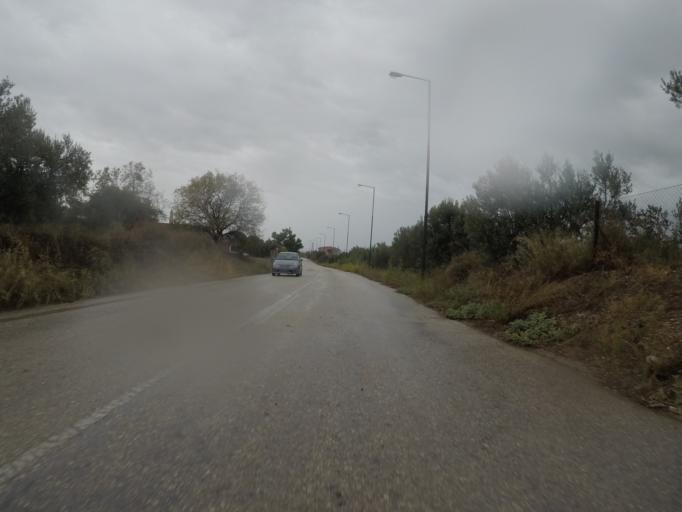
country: GR
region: Peloponnese
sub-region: Nomos Korinthias
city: Arkhaia Korinthos
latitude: 37.8997
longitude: 22.8897
